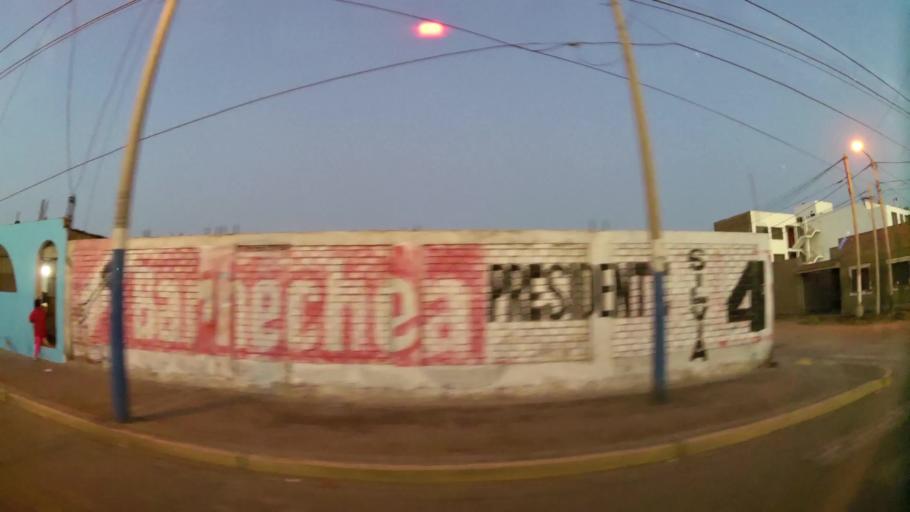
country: PE
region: Ica
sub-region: Provincia de Pisco
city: Pisco
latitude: -13.7150
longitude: -76.2193
